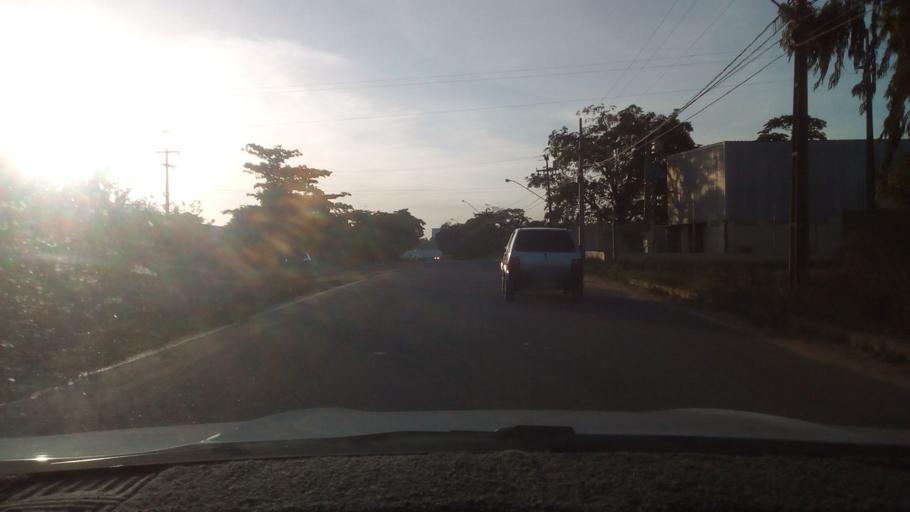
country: BR
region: Paraiba
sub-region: Conde
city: Conde
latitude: -7.1935
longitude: -34.9002
